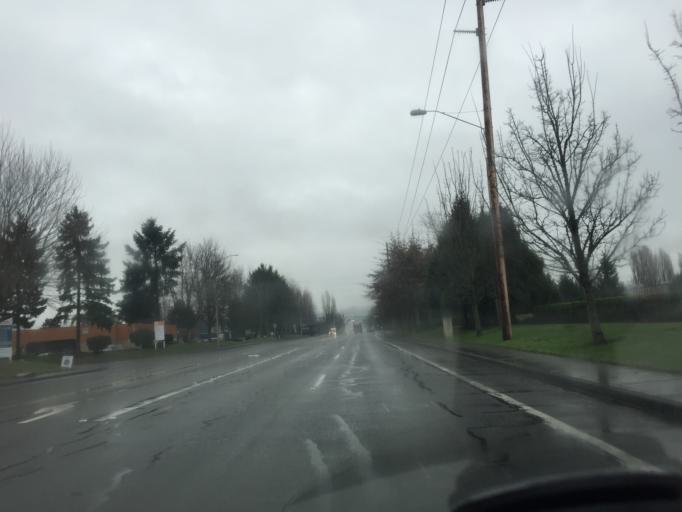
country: US
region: Washington
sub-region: King County
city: SeaTac
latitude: 47.4267
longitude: -122.2522
